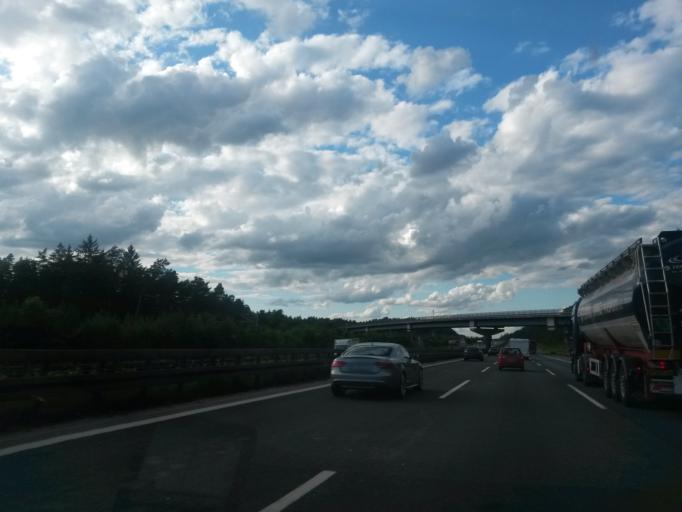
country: DE
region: Bavaria
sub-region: Regierungsbezirk Mittelfranken
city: Schwarzenbruck
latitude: 49.3078
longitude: 11.2080
